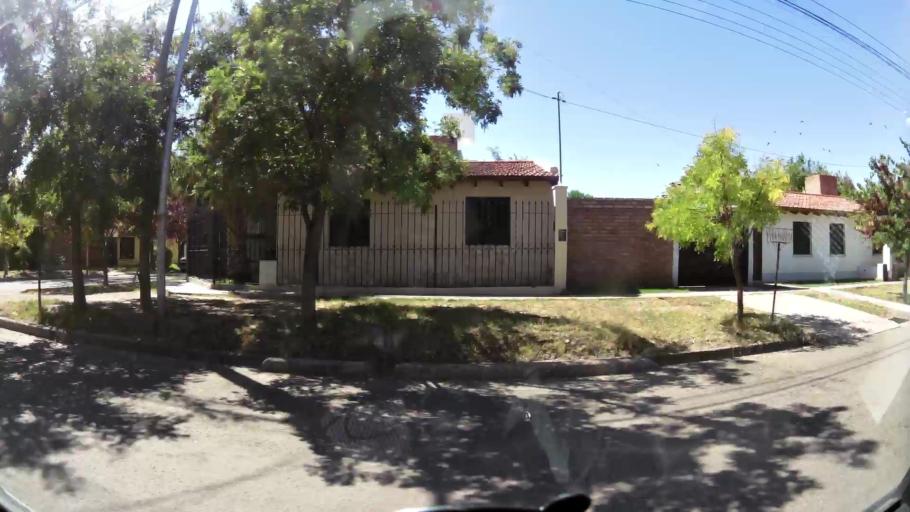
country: AR
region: Mendoza
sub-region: Departamento de Godoy Cruz
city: Godoy Cruz
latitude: -32.9784
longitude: -68.8493
